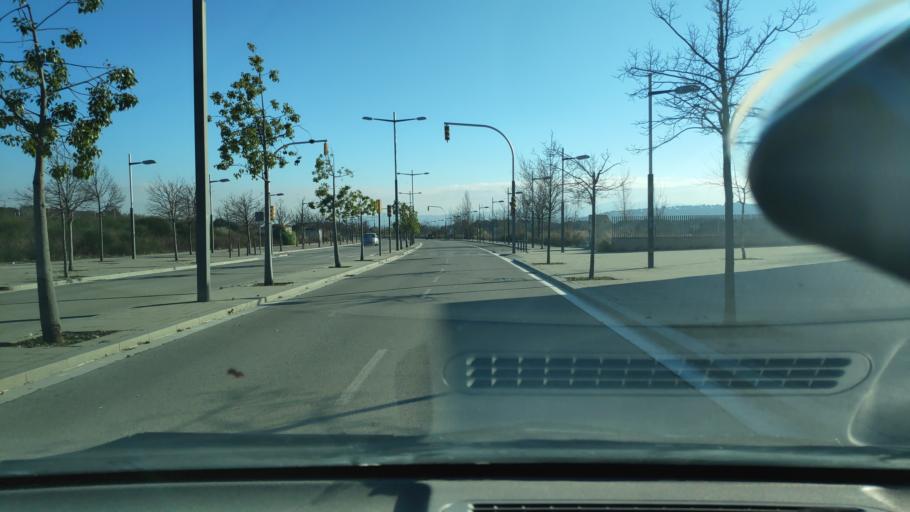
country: ES
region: Catalonia
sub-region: Provincia de Barcelona
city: Sant Quirze del Valles
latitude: 41.5453
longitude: 2.0800
